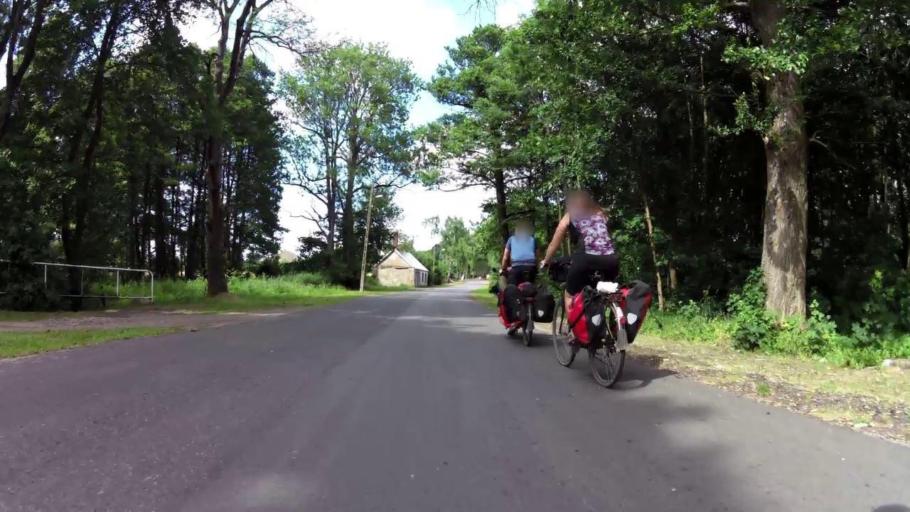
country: PL
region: West Pomeranian Voivodeship
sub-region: Powiat lobeski
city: Lobez
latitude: 53.6240
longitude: 15.6790
